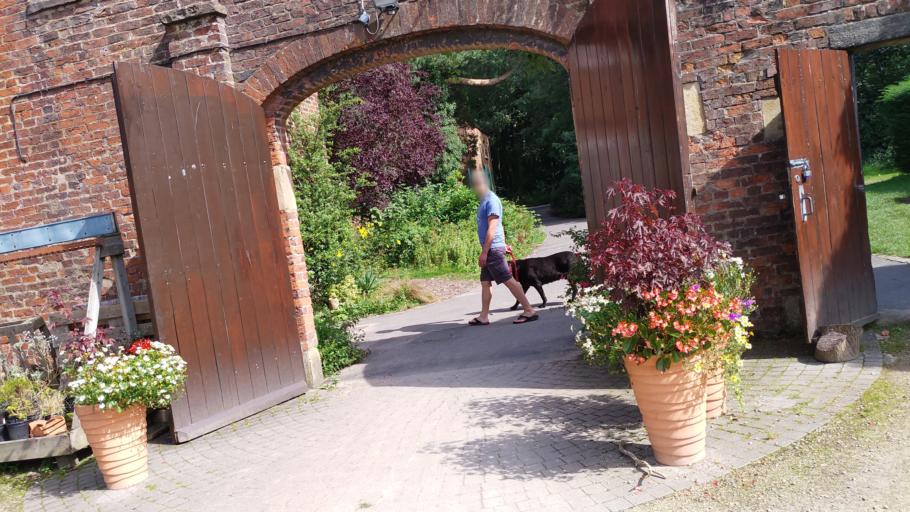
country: GB
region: England
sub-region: Lancashire
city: Leyland
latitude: 53.6829
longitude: -2.7031
